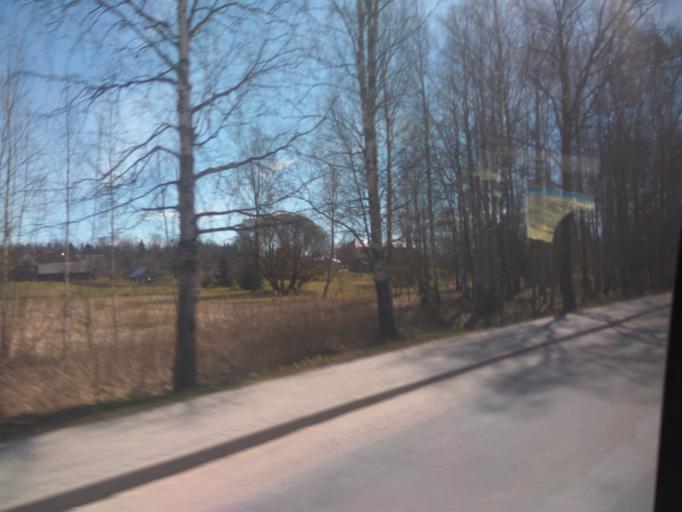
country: LV
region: Aluksnes Rajons
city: Aluksne
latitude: 57.4352
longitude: 27.0387
